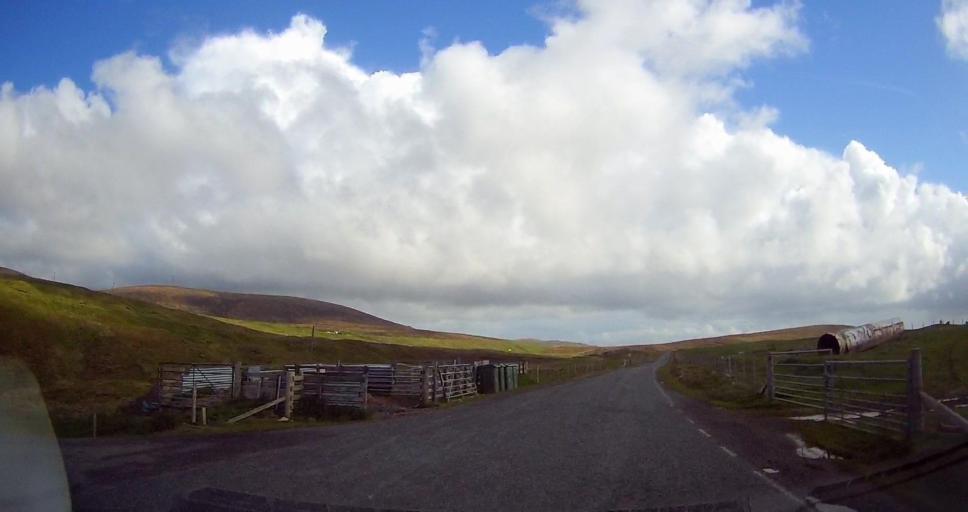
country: GB
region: Scotland
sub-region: Shetland Islands
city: Lerwick
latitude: 60.5120
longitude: -1.3855
